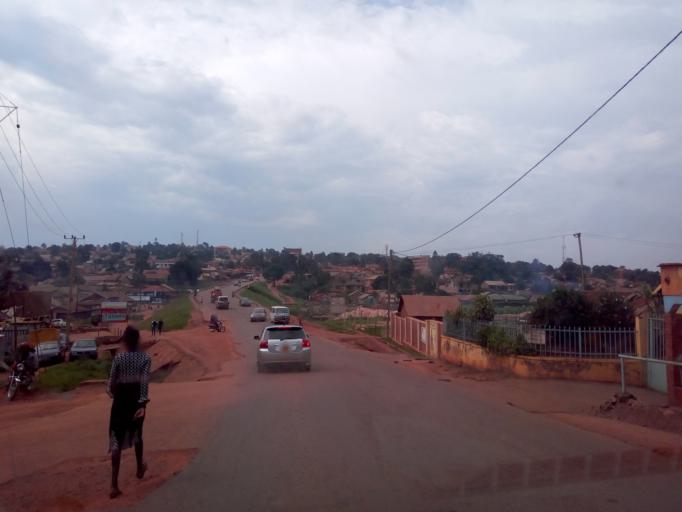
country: UG
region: Central Region
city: Kampala Central Division
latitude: 0.3487
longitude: 32.5789
